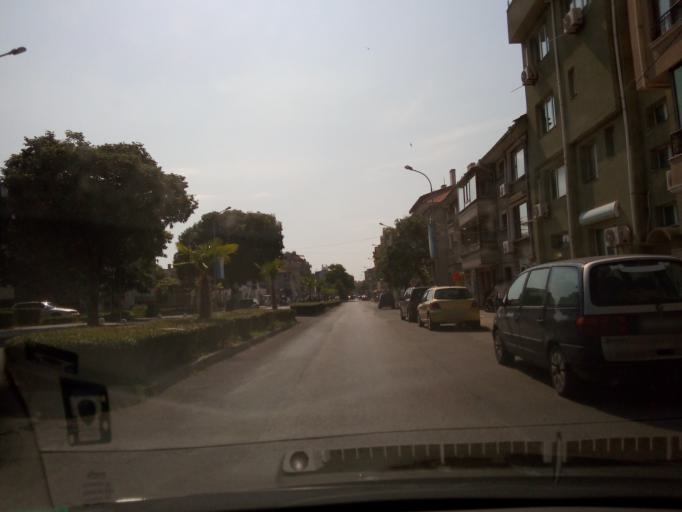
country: BG
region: Burgas
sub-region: Obshtina Pomorie
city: Pomorie
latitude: 42.5612
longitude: 27.6340
